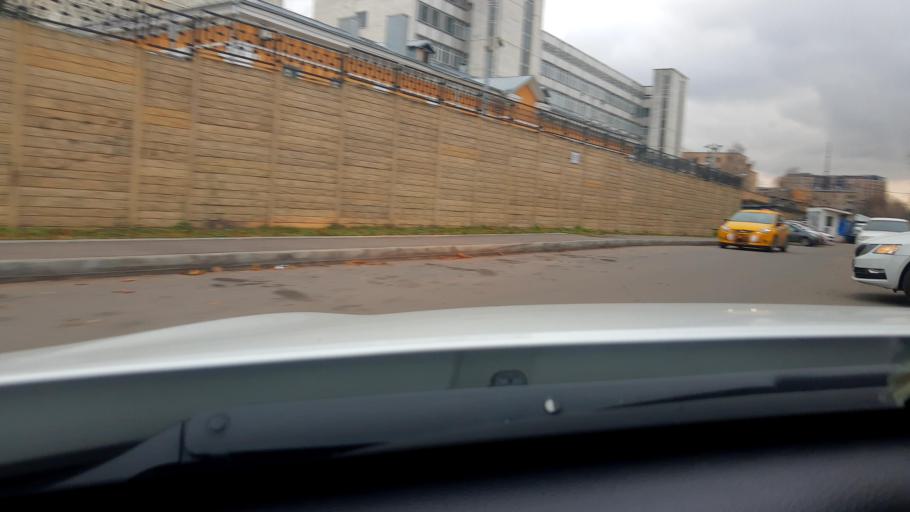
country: RU
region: Moscow
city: Shchukino
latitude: 55.7942
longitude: 37.4625
